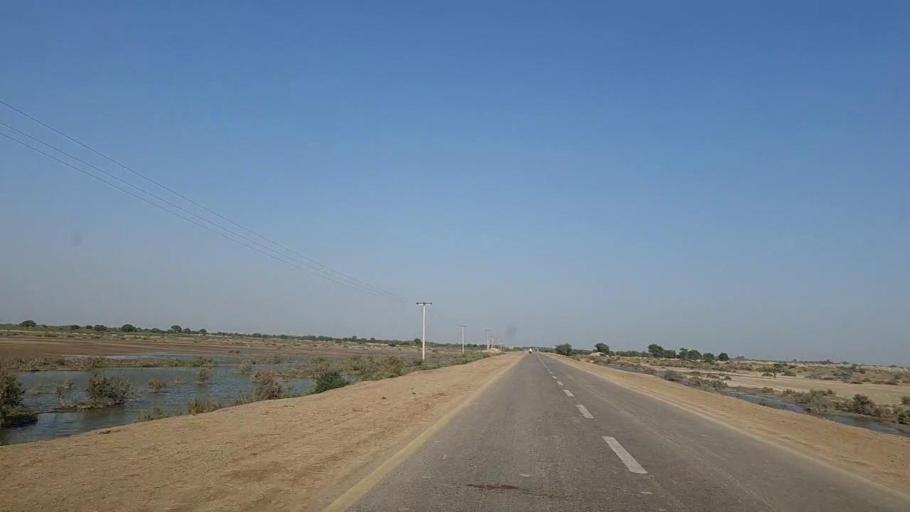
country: PK
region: Sindh
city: Jati
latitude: 24.4569
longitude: 68.3451
